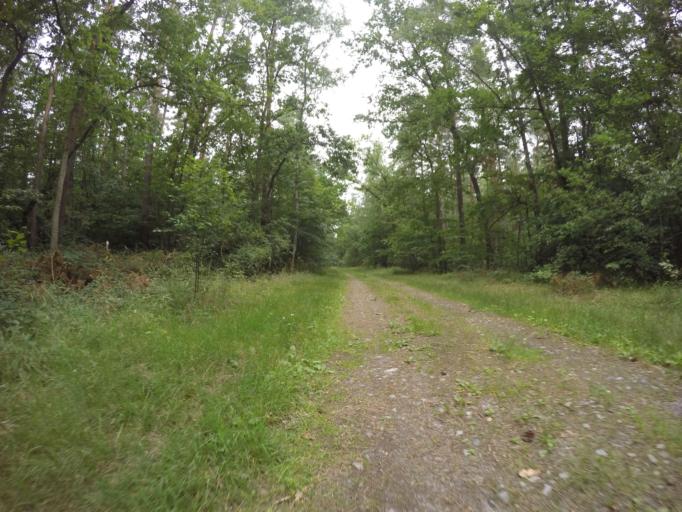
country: DE
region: Lower Saxony
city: Bleckede
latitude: 53.2736
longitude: 10.7140
